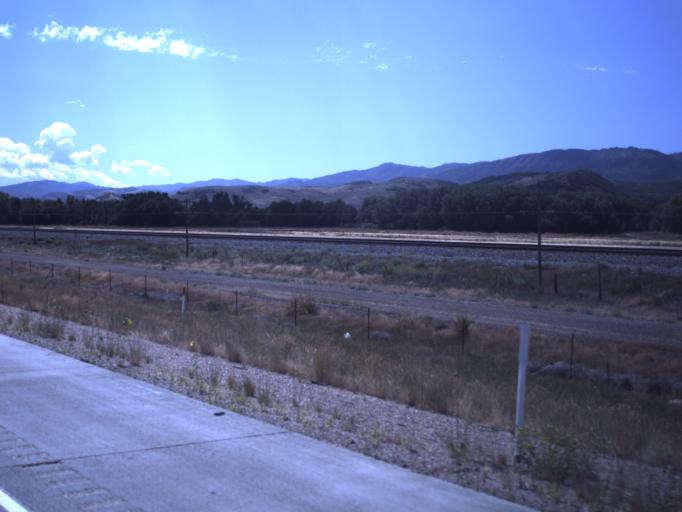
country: US
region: Utah
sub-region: Morgan County
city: Mountain Green
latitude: 41.0931
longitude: -111.7382
